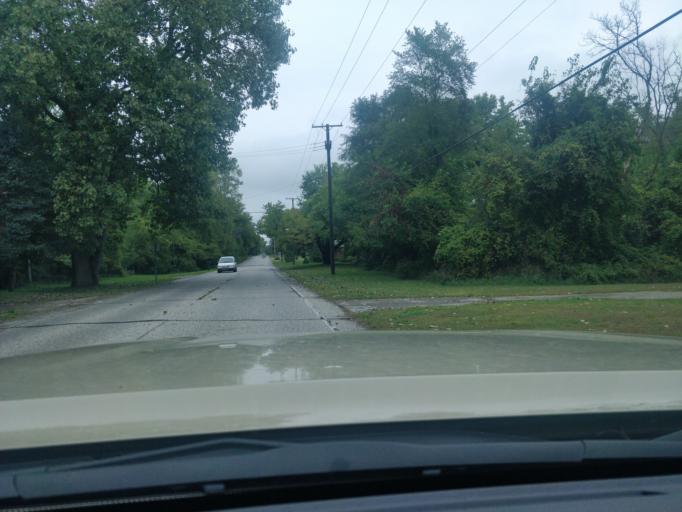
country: US
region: Michigan
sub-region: Wayne County
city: Romulus
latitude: 42.1855
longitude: -83.4189
